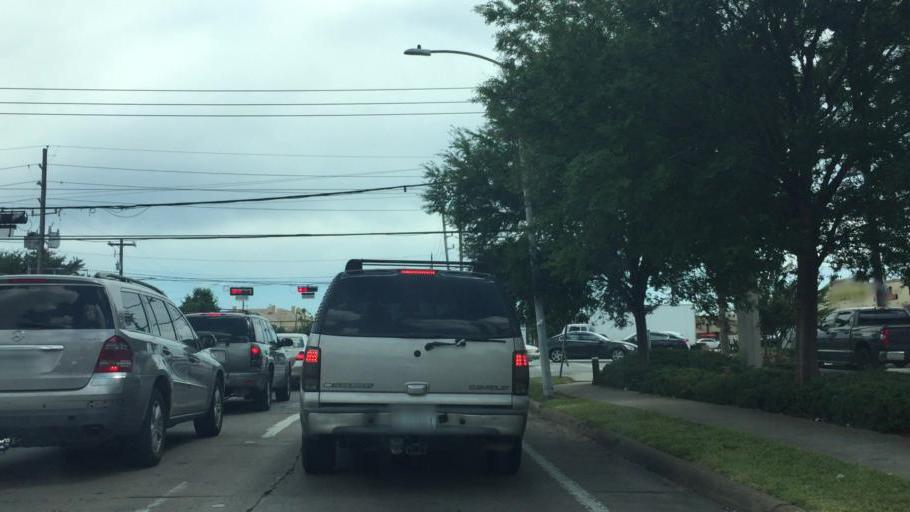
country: US
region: Texas
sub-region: Harris County
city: Bunker Hill Village
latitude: 29.7369
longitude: -95.5888
